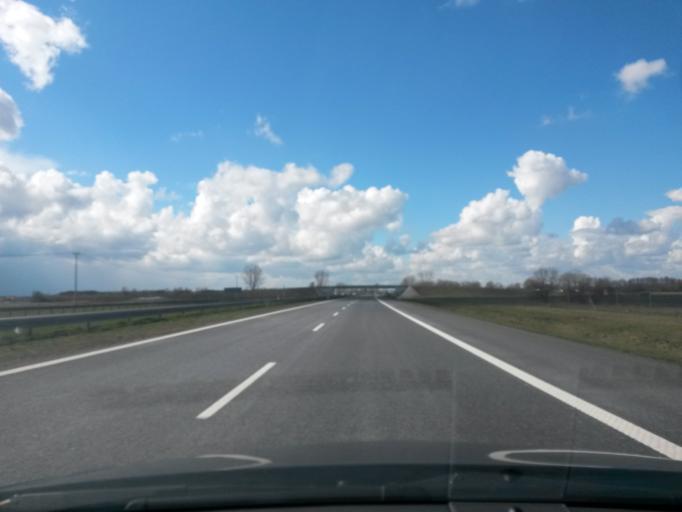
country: PL
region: Lodz Voivodeship
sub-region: Powiat poddebicki
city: Wartkowice
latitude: 52.0030
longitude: 18.9930
